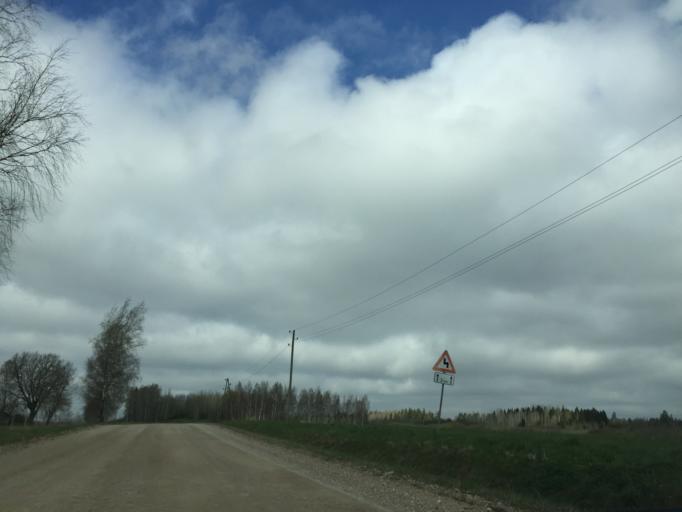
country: EE
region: Valgamaa
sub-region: Valga linn
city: Valga
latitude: 57.5600
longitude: 26.2779
